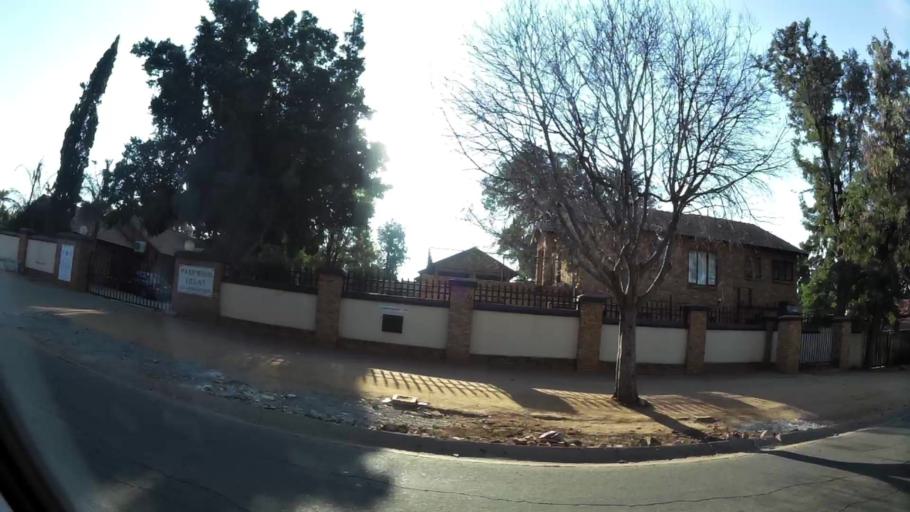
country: ZA
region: North-West
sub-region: Bojanala Platinum District Municipality
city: Rustenburg
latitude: -25.6768
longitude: 27.2351
